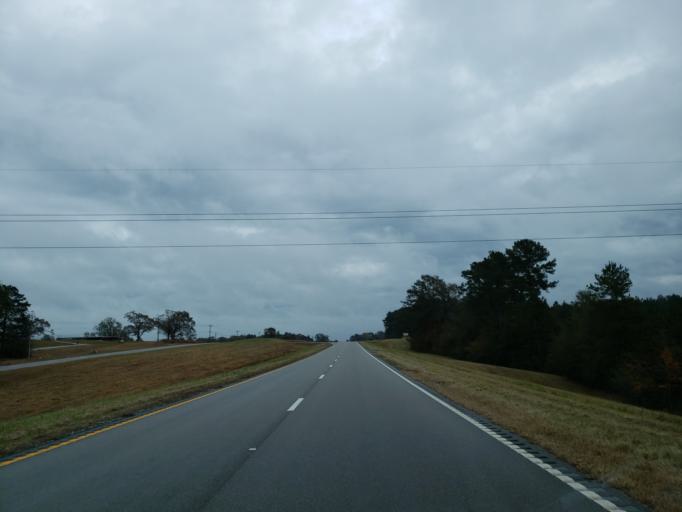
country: US
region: Mississippi
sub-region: Wayne County
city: Waynesboro
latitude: 31.6955
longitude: -88.7382
